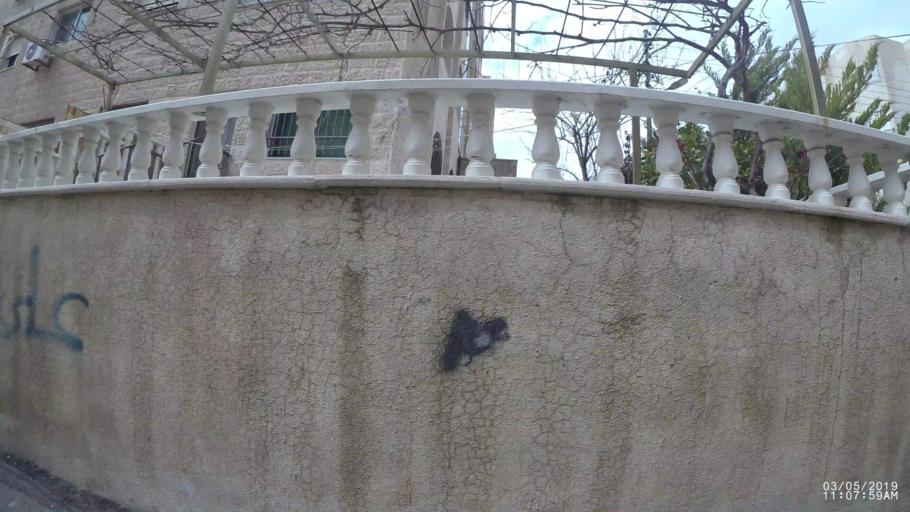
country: JO
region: Amman
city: Amman
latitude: 31.9895
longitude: 35.9218
